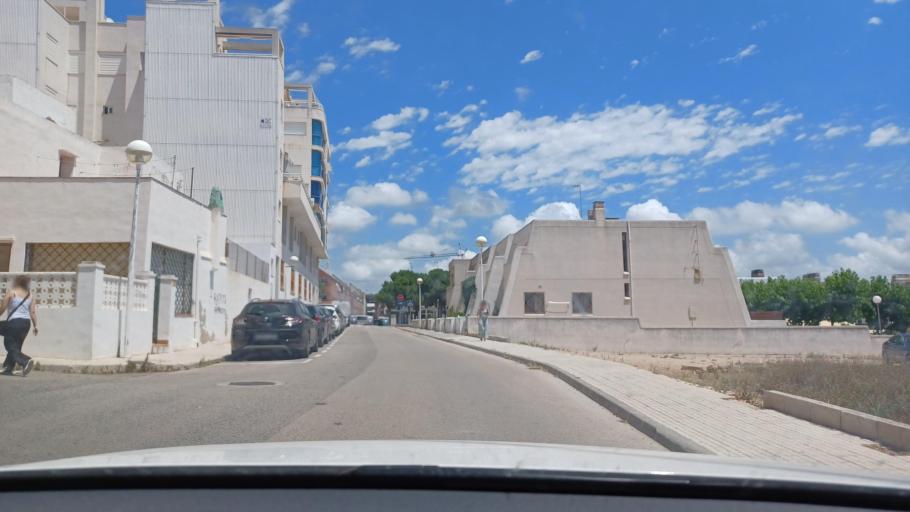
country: ES
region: Catalonia
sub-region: Provincia de Tarragona
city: Sant Carles de la Rapita
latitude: 40.6141
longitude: 0.5895
